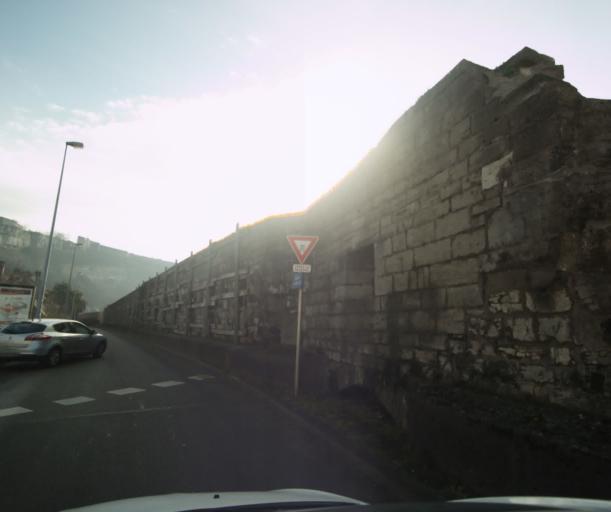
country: FR
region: Franche-Comte
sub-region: Departement du Doubs
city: Besancon
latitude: 47.2311
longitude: 6.0243
